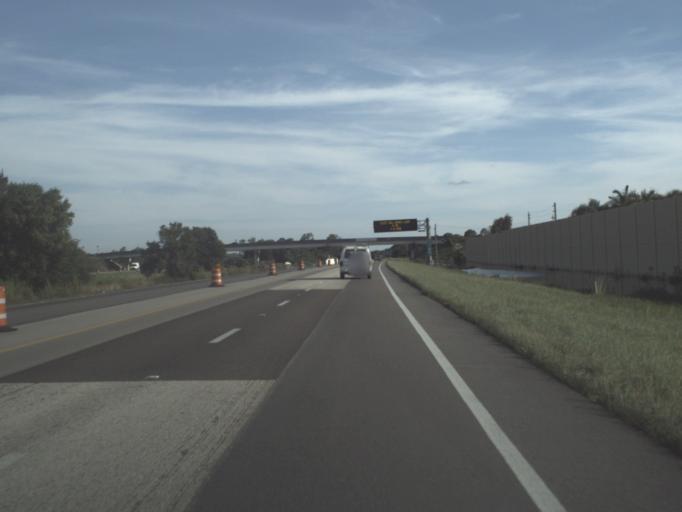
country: US
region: Florida
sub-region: Charlotte County
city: Harbour Heights
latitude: 27.0053
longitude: -82.0395
